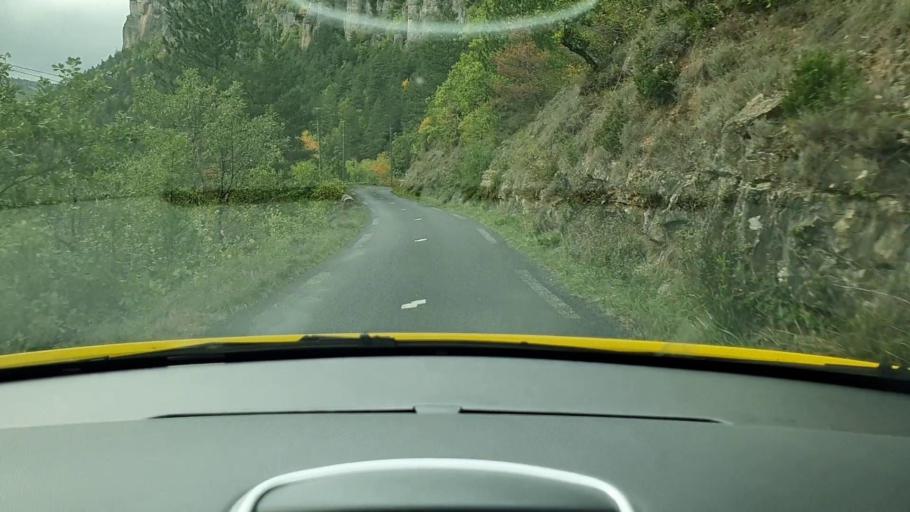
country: FR
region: Languedoc-Roussillon
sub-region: Departement de la Lozere
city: Meyrueis
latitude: 44.0891
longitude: 3.3965
